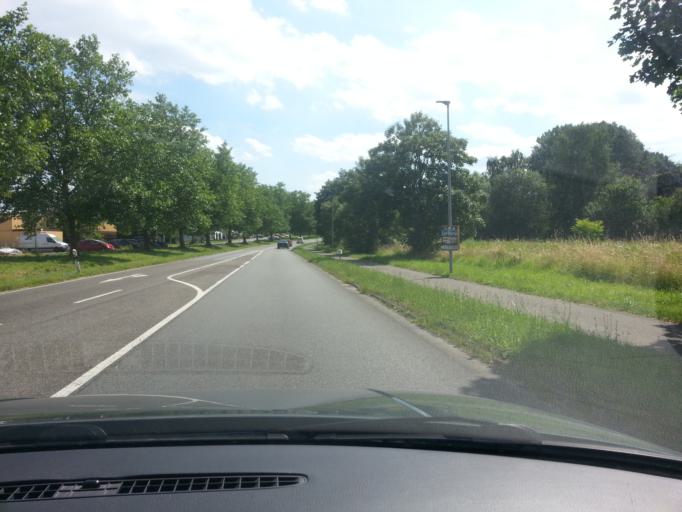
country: DE
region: Saarland
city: Blieskastel
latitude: 49.2347
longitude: 7.2698
